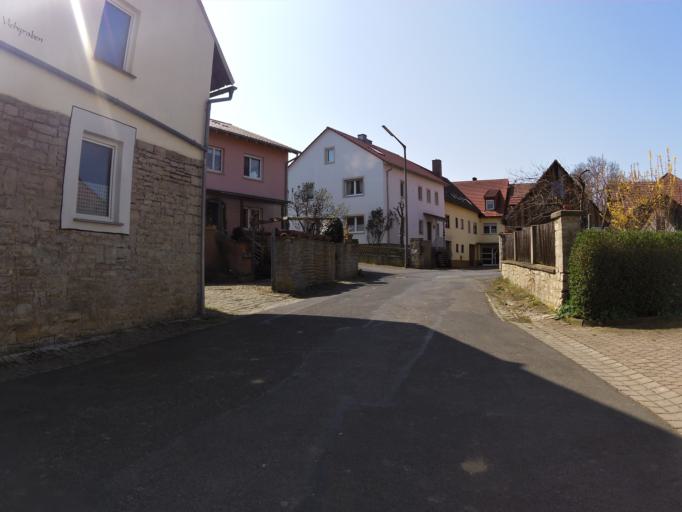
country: DE
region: Bavaria
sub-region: Regierungsbezirk Unterfranken
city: Dettelbach
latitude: 49.8184
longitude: 10.1509
